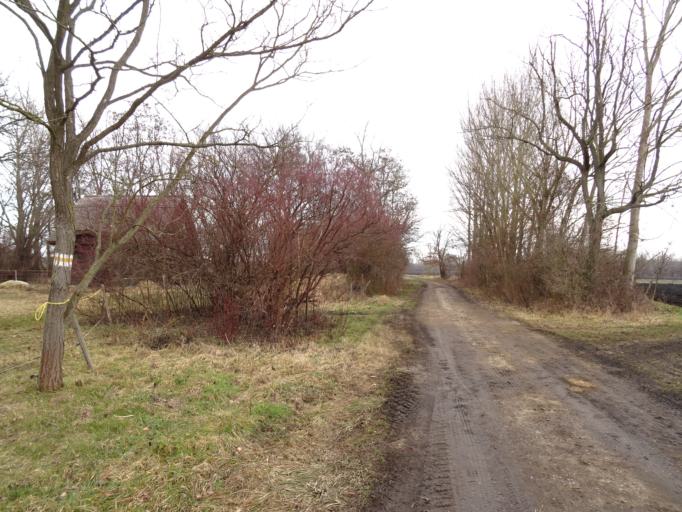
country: HU
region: Gyor-Moson-Sopron
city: Kony
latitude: 47.6868
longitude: 17.3527
